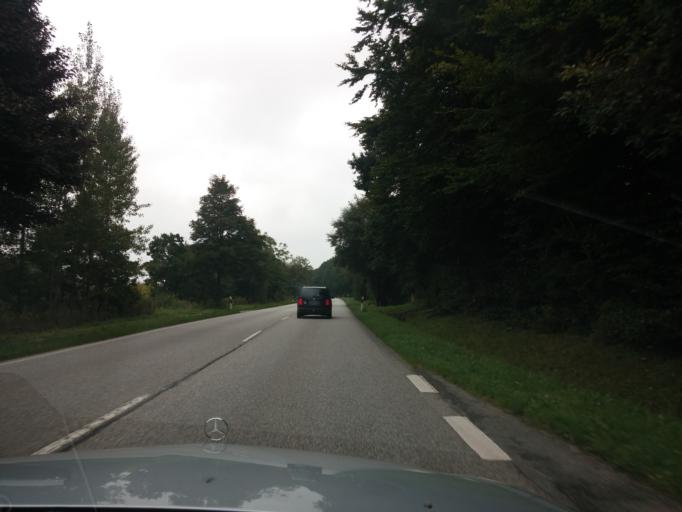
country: DE
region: Schleswig-Holstein
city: Silberstedt
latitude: 54.5161
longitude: 9.3541
